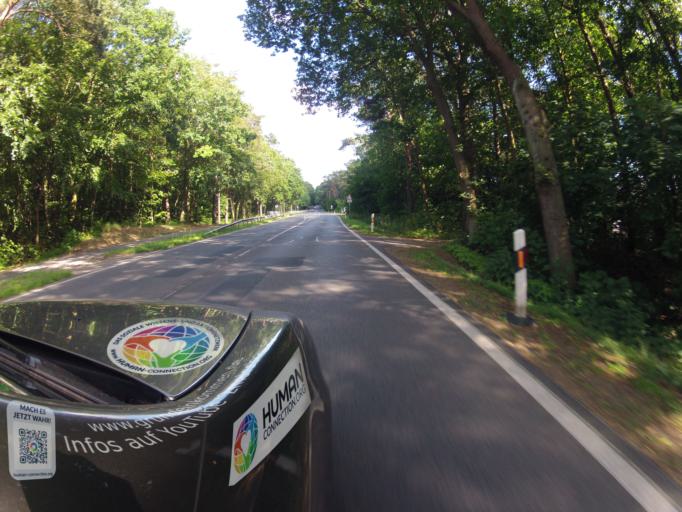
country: DE
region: Mecklenburg-Vorpommern
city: Koserow
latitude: 54.0391
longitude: 14.0134
